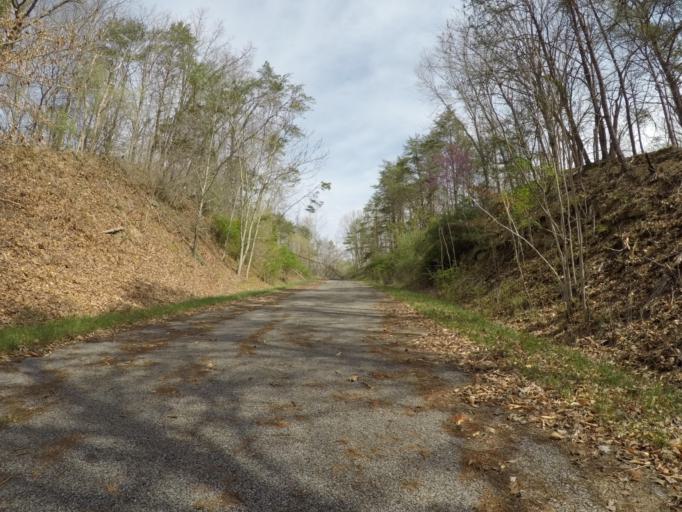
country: US
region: West Virginia
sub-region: Wayne County
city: Lavalette
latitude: 38.3130
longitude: -82.3513
